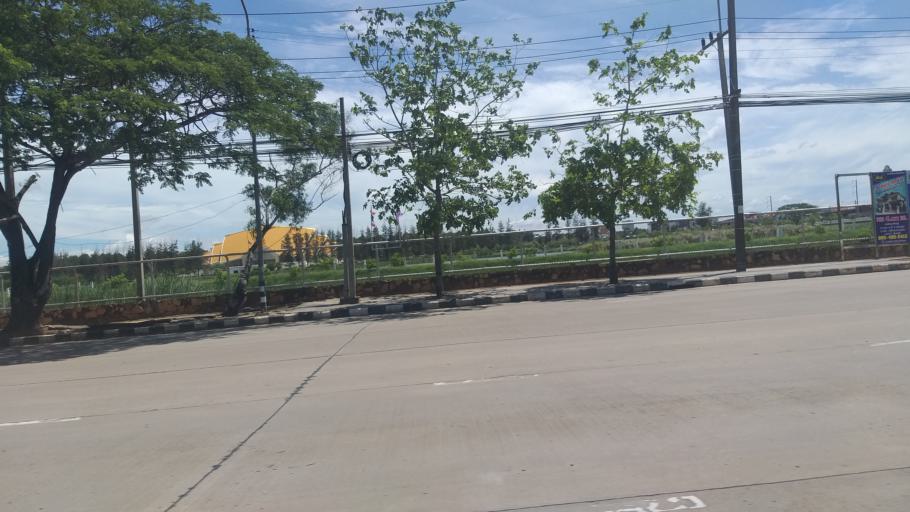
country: TH
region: Khon Kaen
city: Khon Kaen
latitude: 16.4413
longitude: 102.8175
